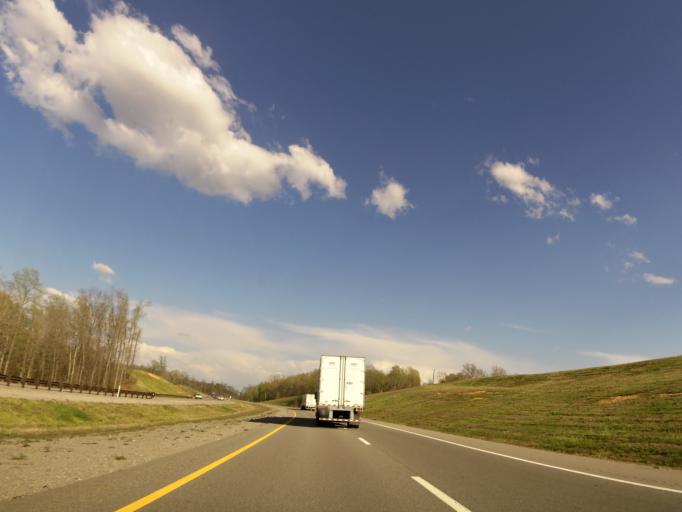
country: US
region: Tennessee
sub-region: Williamson County
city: Thompson's Station
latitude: 35.8252
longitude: -87.0524
